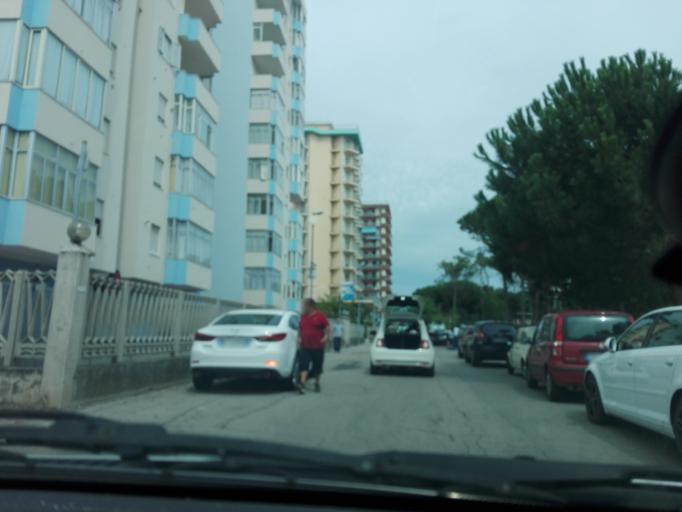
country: IT
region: Abruzzo
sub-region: Provincia di Pescara
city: Villa Raspa
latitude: 42.4965
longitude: 14.1810
